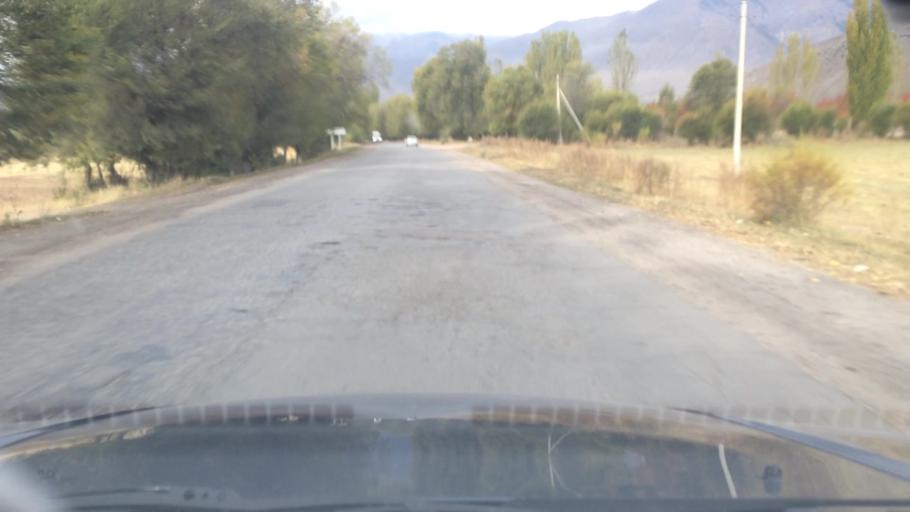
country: KG
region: Ysyk-Koel
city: Tyup
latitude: 42.7843
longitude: 78.2760
